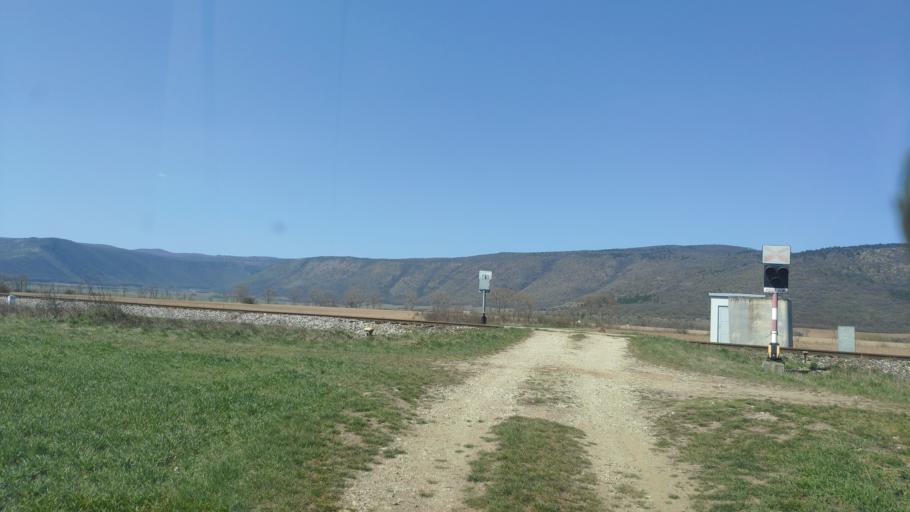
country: SK
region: Kosicky
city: Moldava nad Bodvou
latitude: 48.6044
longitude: 20.9265
